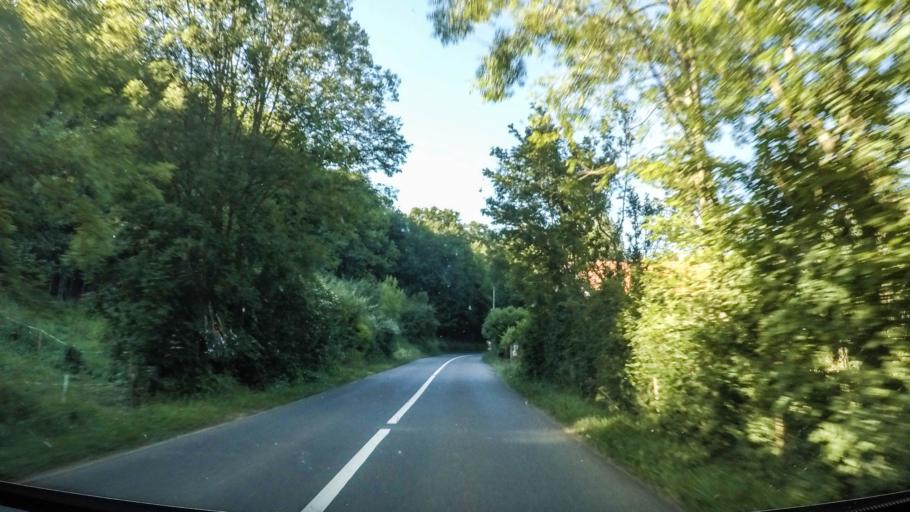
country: FR
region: Midi-Pyrenees
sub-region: Departement de l'Aveyron
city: Marcillac-Vallon
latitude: 44.4753
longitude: 2.4532
